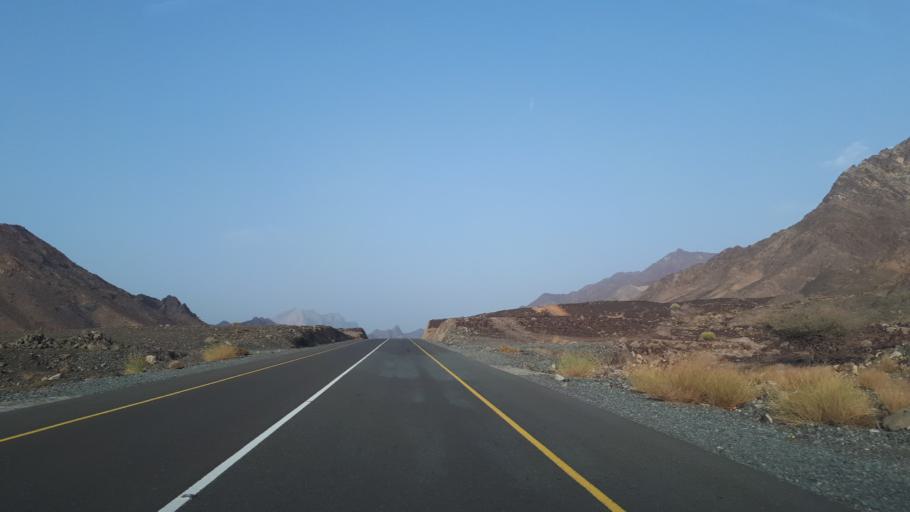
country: OM
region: Az Zahirah
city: Yanqul
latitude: 23.4951
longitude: 56.8888
